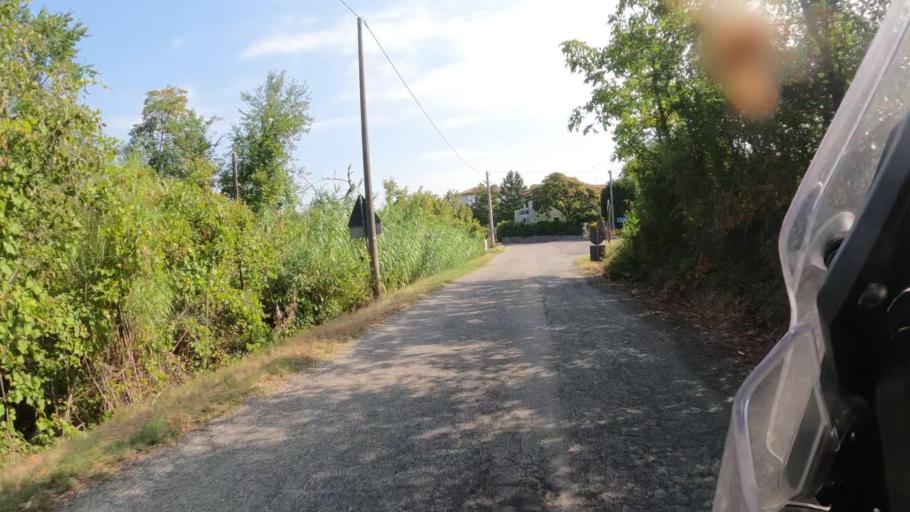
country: IT
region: Piedmont
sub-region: Provincia di Alessandria
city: Altavilla Monferrato
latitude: 44.9667
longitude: 8.3862
